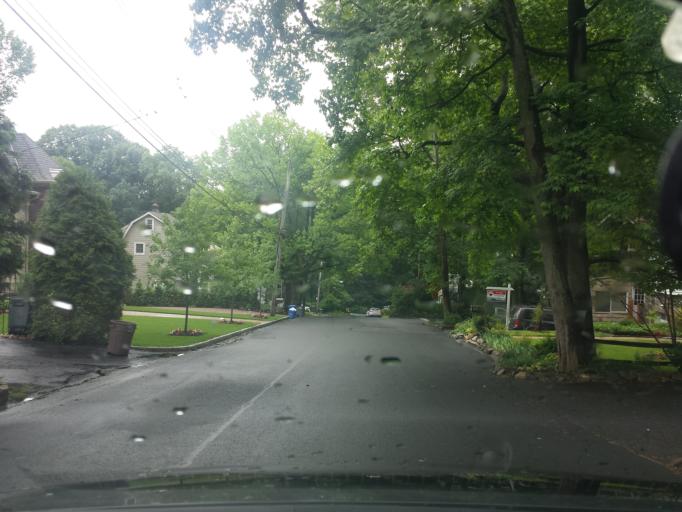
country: US
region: New York
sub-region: Richmond County
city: Staten Island
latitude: 40.5816
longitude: -74.1263
